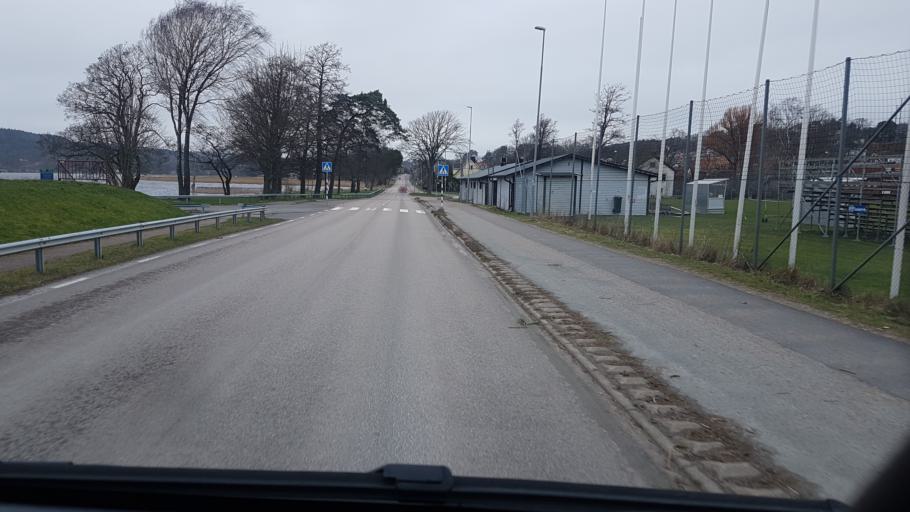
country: SE
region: Vaestra Goetaland
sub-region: Lerums Kommun
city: Lerum
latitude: 57.7676
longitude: 12.2534
